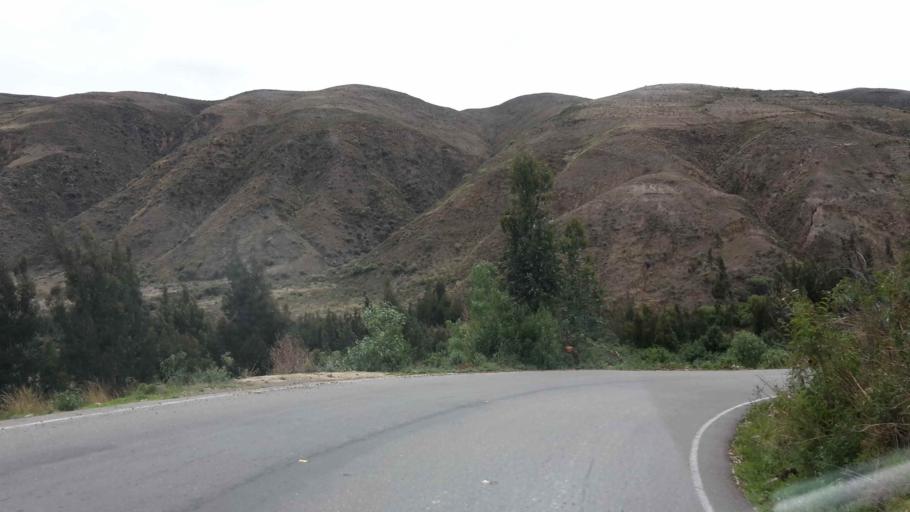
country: BO
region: Cochabamba
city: Colomi
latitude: -17.4109
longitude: -65.7834
